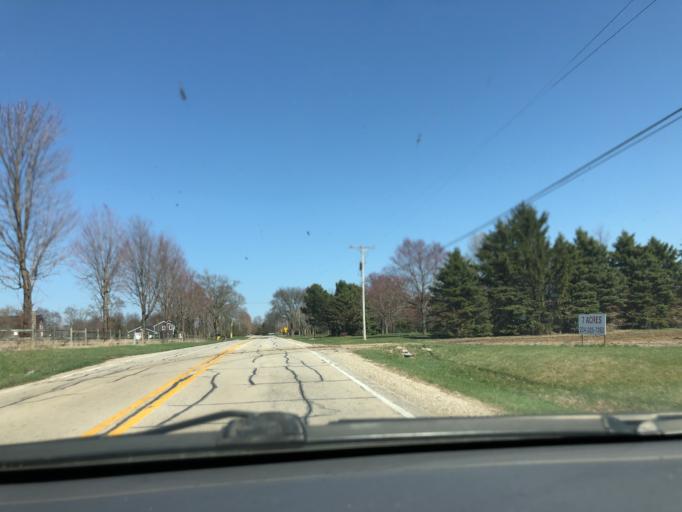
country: US
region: Illinois
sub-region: McHenry County
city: Huntley
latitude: 42.1610
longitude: -88.4885
